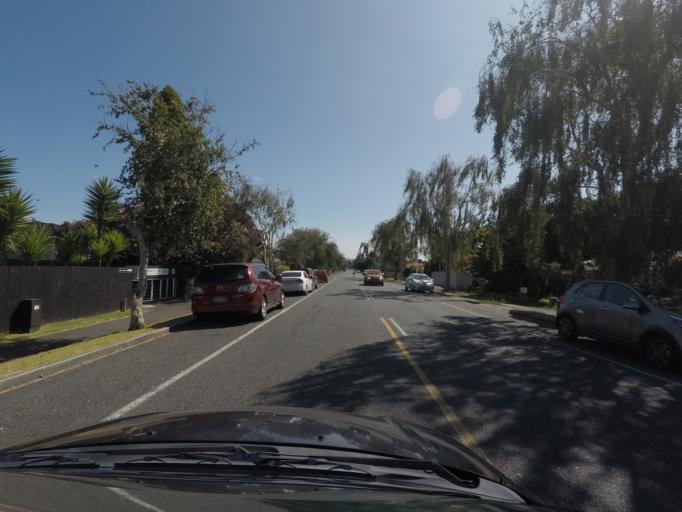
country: NZ
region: Auckland
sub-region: Auckland
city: Rosebank
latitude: -36.8876
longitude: 174.6844
